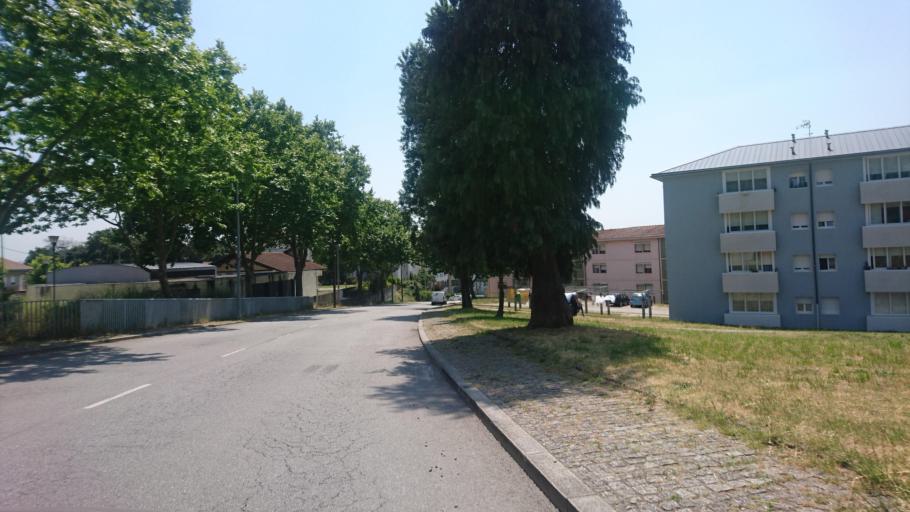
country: PT
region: Porto
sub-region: Gondomar
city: Rio Tinto
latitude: 41.1609
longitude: -8.5672
